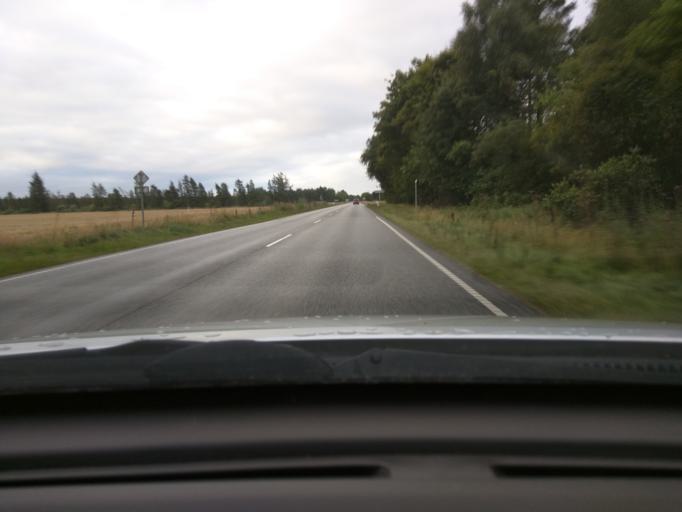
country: DK
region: Central Jutland
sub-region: Ikast-Brande Kommune
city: Bording Kirkeby
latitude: 56.2158
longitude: 9.3183
